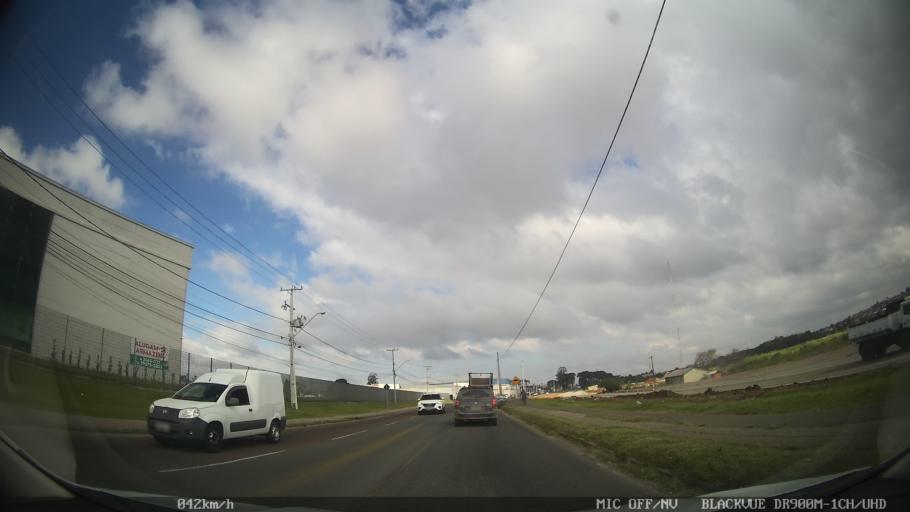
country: BR
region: Parana
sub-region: Pinhais
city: Pinhais
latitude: -25.4071
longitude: -49.1894
